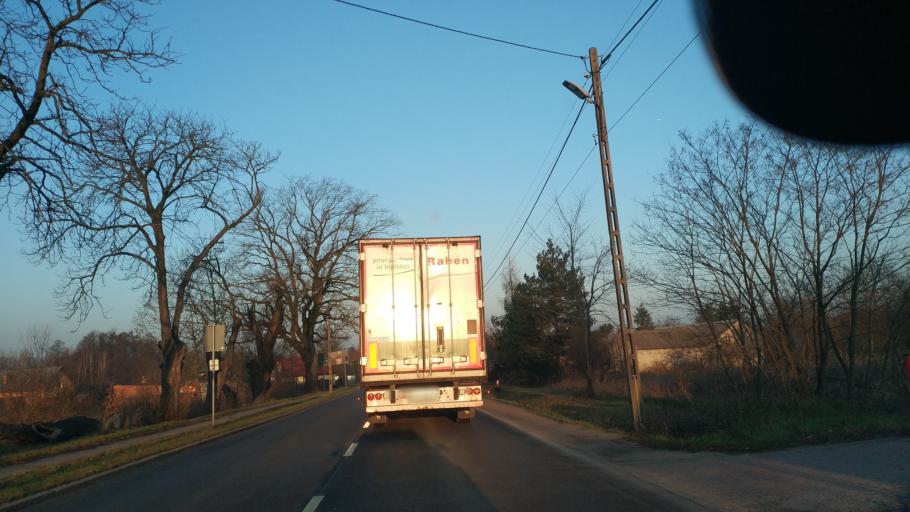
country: PL
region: Masovian Voivodeship
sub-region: Powiat pruszkowski
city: Owczarnia
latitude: 52.0742
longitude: 20.7012
